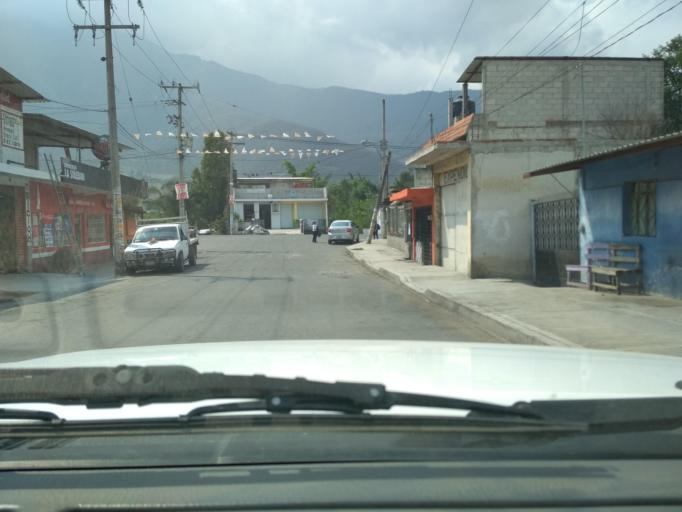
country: MX
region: Veracruz
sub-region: Acultzingo
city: Acatla
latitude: 18.7605
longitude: -97.2276
